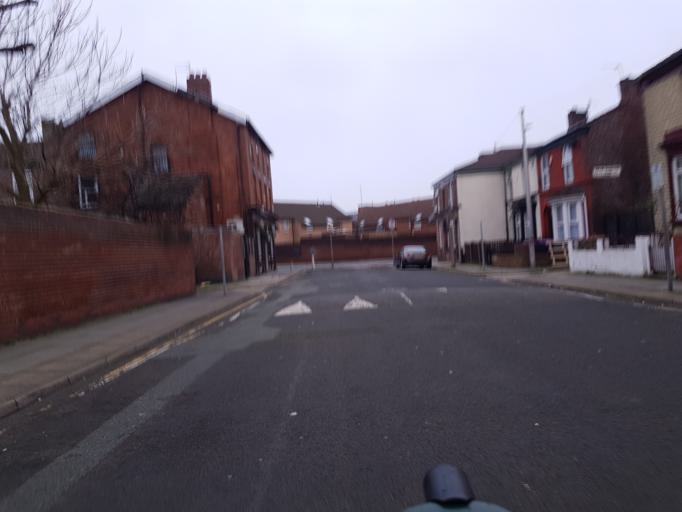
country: GB
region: England
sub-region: Liverpool
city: Liverpool
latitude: 53.4384
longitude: -2.9740
